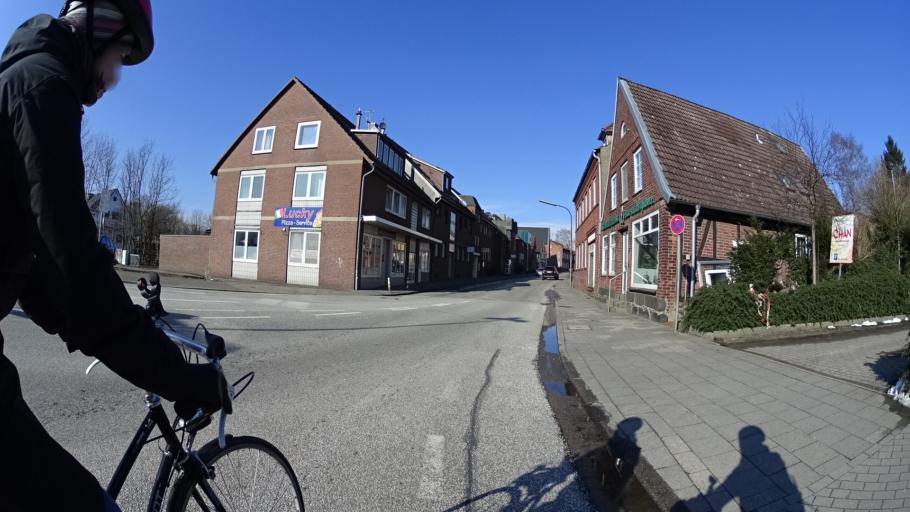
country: DE
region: Schleswig-Holstein
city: Preetz
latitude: 54.2355
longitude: 10.2853
